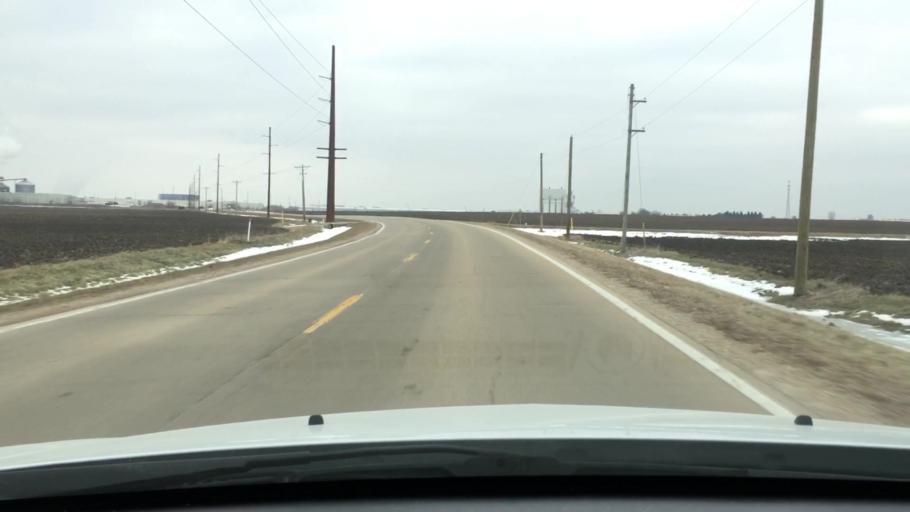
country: US
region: Illinois
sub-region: Ogle County
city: Rochelle
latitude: 41.8827
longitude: -89.0252
